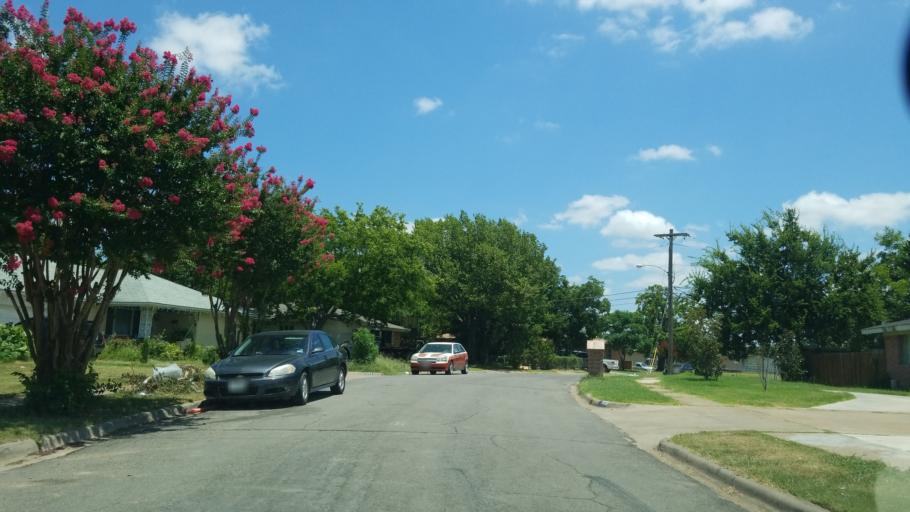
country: US
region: Texas
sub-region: Dallas County
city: Balch Springs
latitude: 32.7394
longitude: -96.7041
